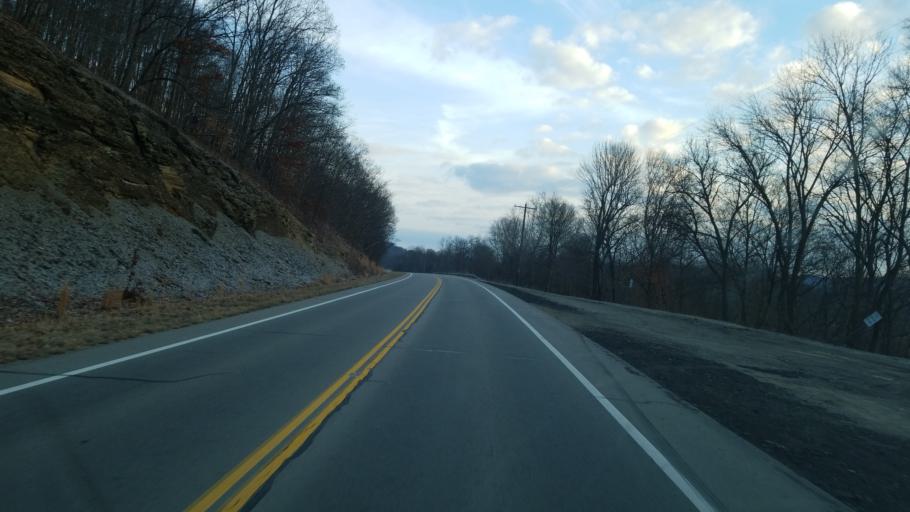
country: US
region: Ohio
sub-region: Ross County
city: Frankfort
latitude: 39.3013
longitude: -83.1374
